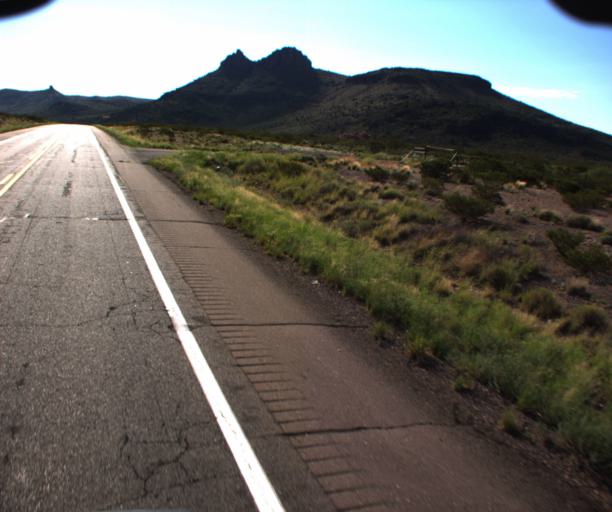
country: US
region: Arizona
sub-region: Greenlee County
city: Clifton
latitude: 32.8464
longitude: -109.3759
